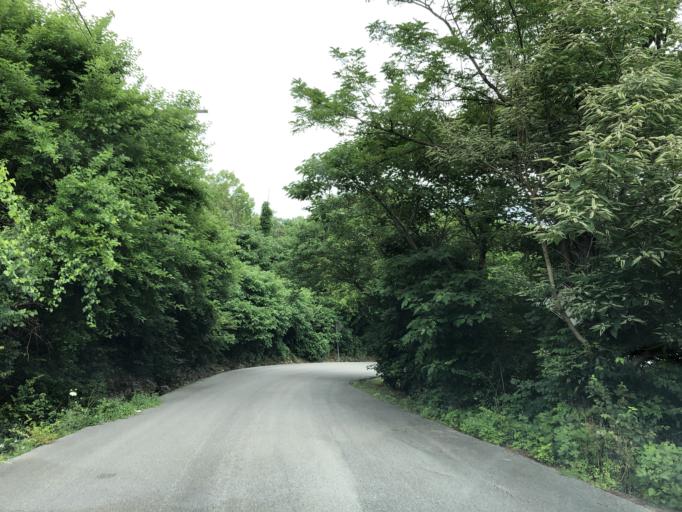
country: US
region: Tennessee
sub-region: Davidson County
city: Goodlettsville
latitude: 36.2837
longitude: -86.7093
